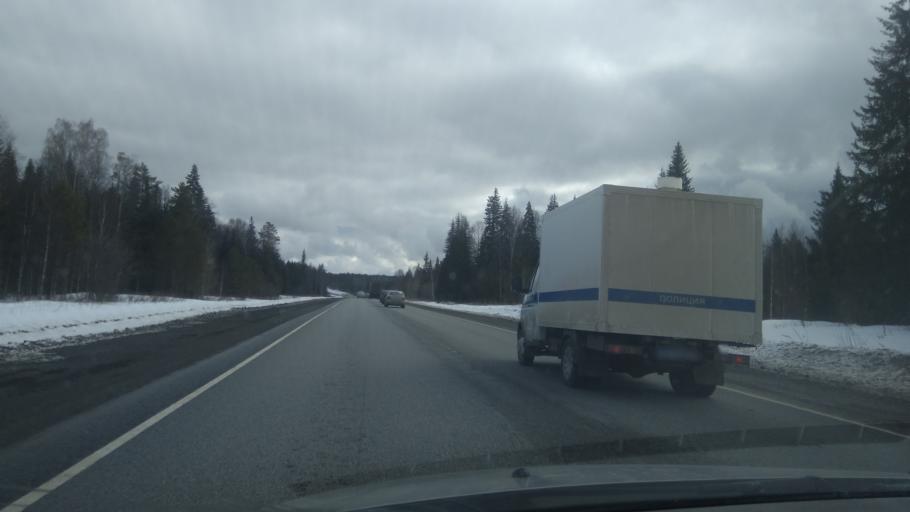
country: RU
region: Sverdlovsk
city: Atig
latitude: 56.8097
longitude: 59.3653
